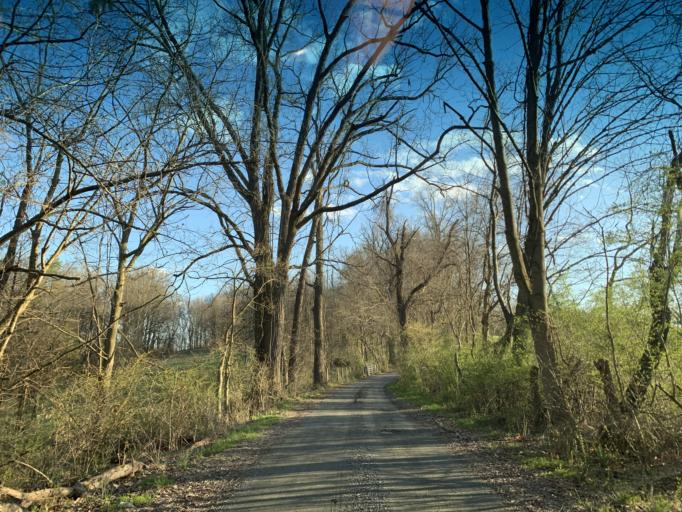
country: US
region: Maryland
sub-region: Harford County
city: Aberdeen
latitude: 39.6140
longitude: -76.2190
